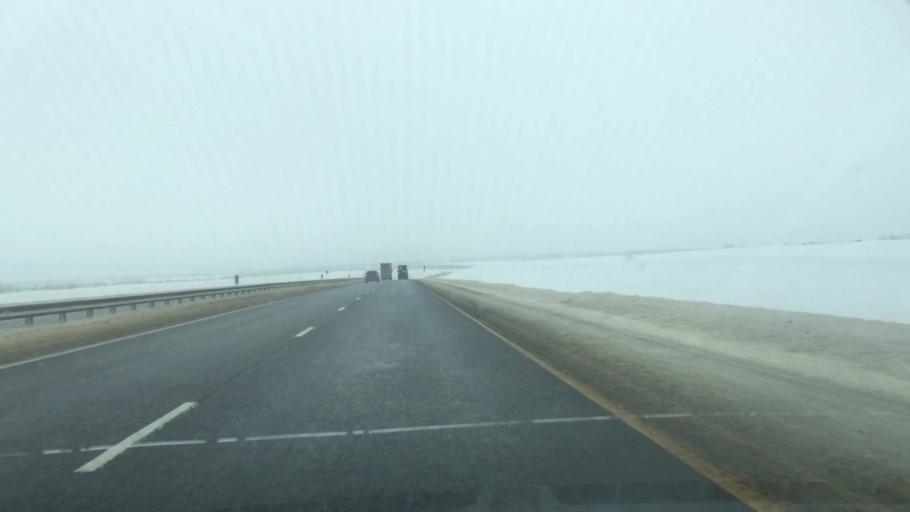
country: RU
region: Lipetsk
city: Stanovoye
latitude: 52.7931
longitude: 38.3427
